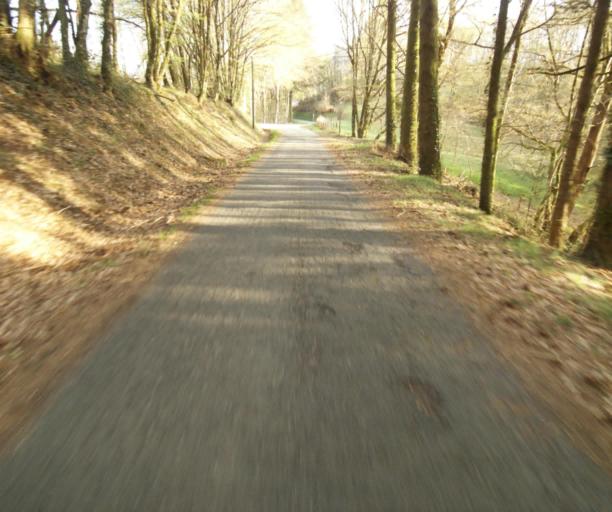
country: FR
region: Limousin
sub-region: Departement de la Correze
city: Correze
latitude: 45.3822
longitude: 1.8411
